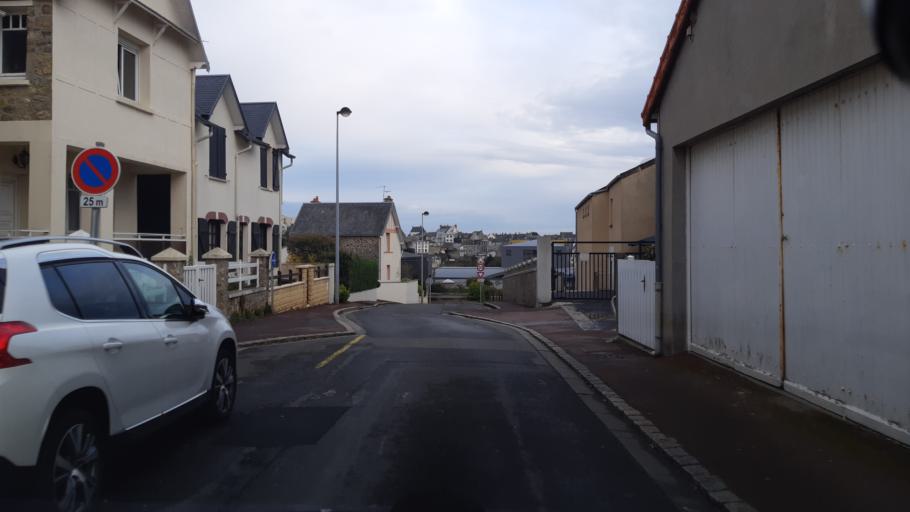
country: FR
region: Lower Normandy
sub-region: Departement de la Manche
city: Granville
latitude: 48.8414
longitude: -1.5909
